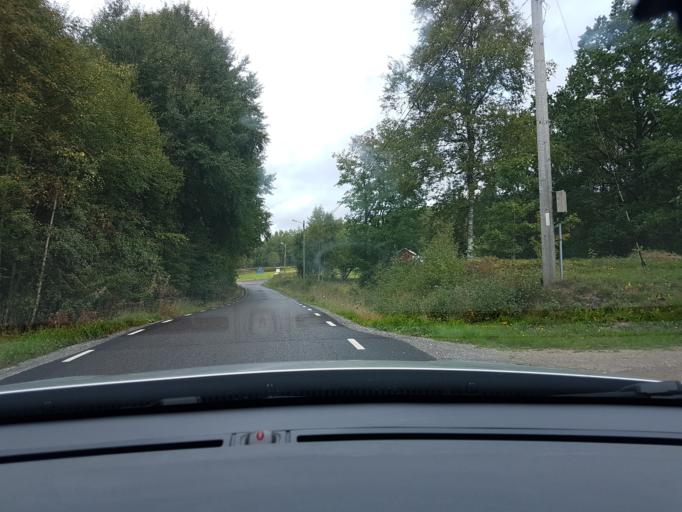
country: SE
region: Vaestra Goetaland
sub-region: Ale Kommun
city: Skepplanda
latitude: 57.8954
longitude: 12.1938
